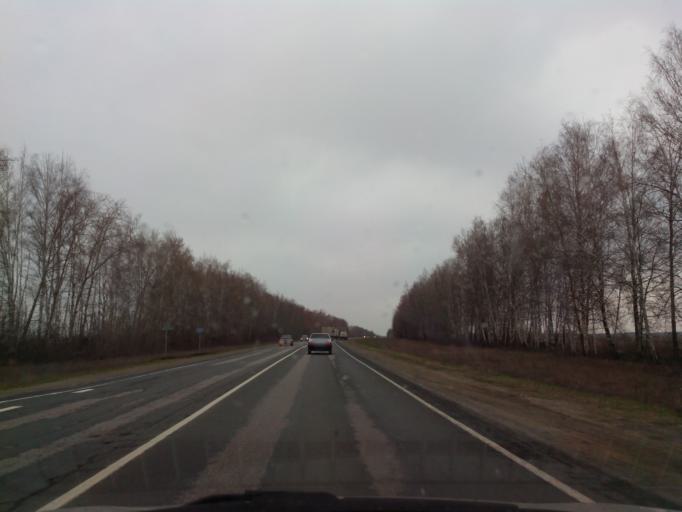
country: RU
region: Tambov
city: Pervomayskiy
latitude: 53.0949
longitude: 40.3966
